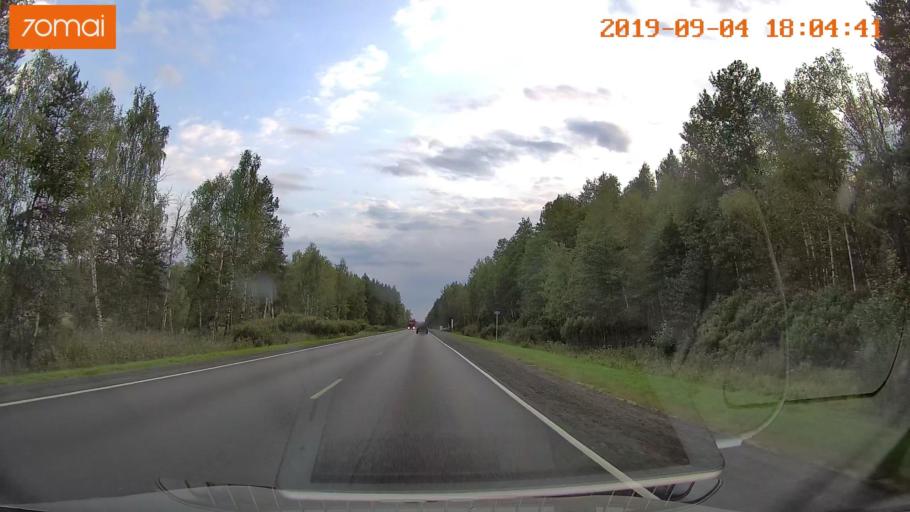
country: RU
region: Moskovskaya
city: Il'inskiy Pogost
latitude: 55.4494
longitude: 38.8358
